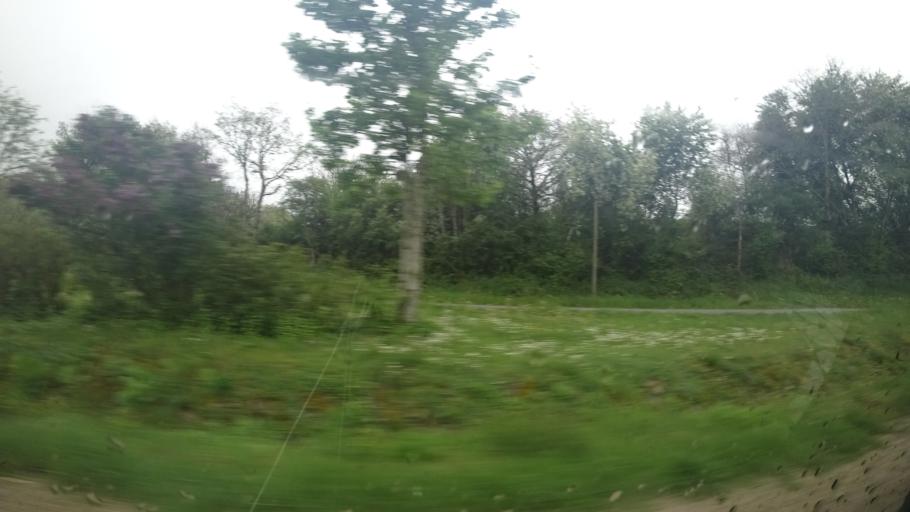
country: FR
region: Midi-Pyrenees
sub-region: Departement de l'Aveyron
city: Laissac
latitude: 44.2775
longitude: 2.8627
